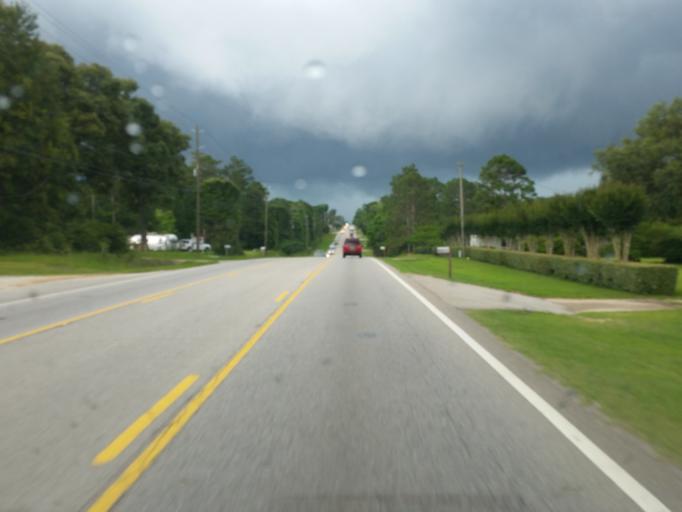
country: US
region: Mississippi
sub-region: Jackson County
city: Hurley
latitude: 30.7943
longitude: -88.3124
